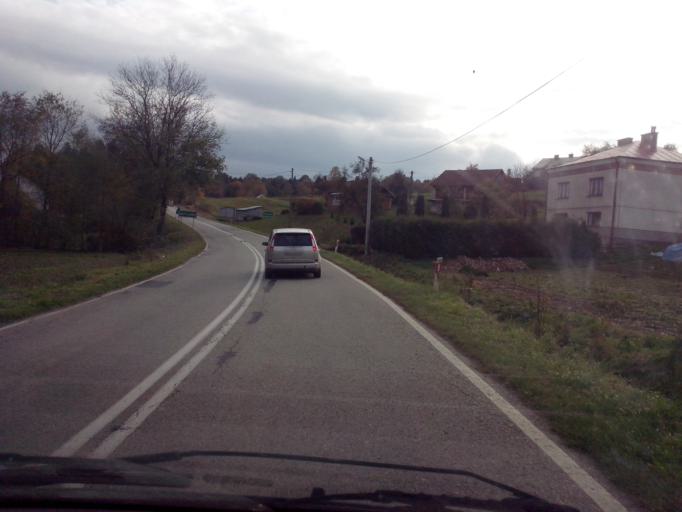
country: PL
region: Subcarpathian Voivodeship
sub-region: Powiat strzyzowski
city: Wisniowa
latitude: 49.8819
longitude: 21.6457
